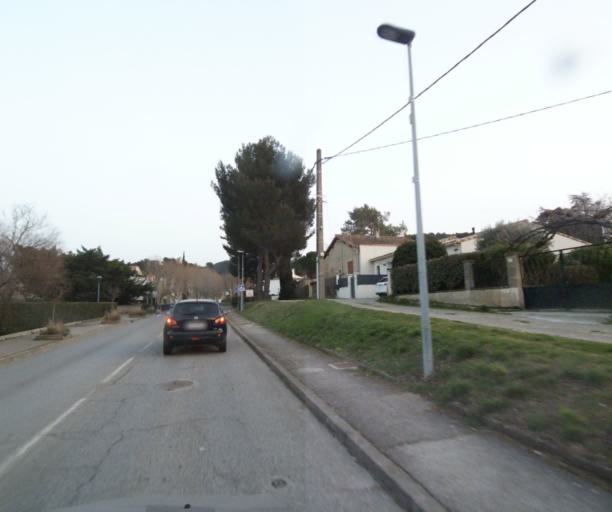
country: FR
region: Provence-Alpes-Cote d'Azur
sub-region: Departement des Bouches-du-Rhone
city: Simiane-Collongue
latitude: 43.4313
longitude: 5.4340
